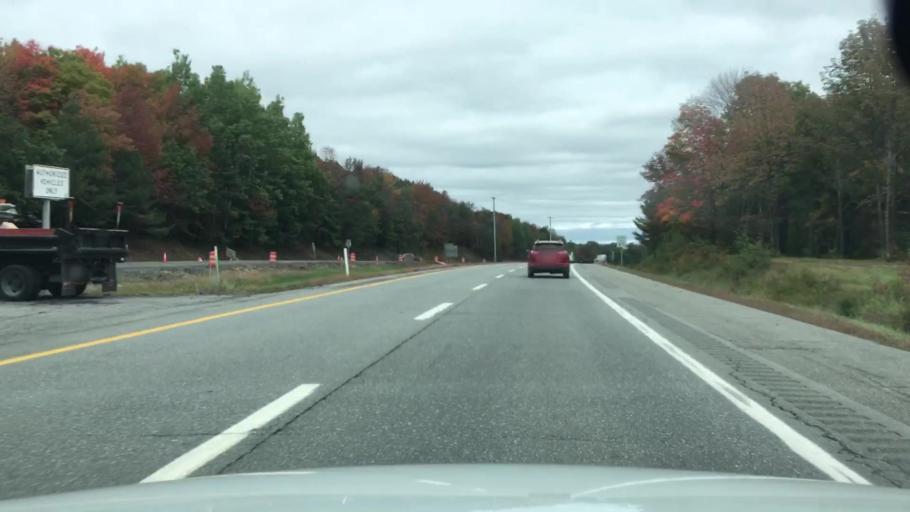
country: US
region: Maine
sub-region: Somerset County
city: Fairfield
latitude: 44.5996
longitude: -69.6080
